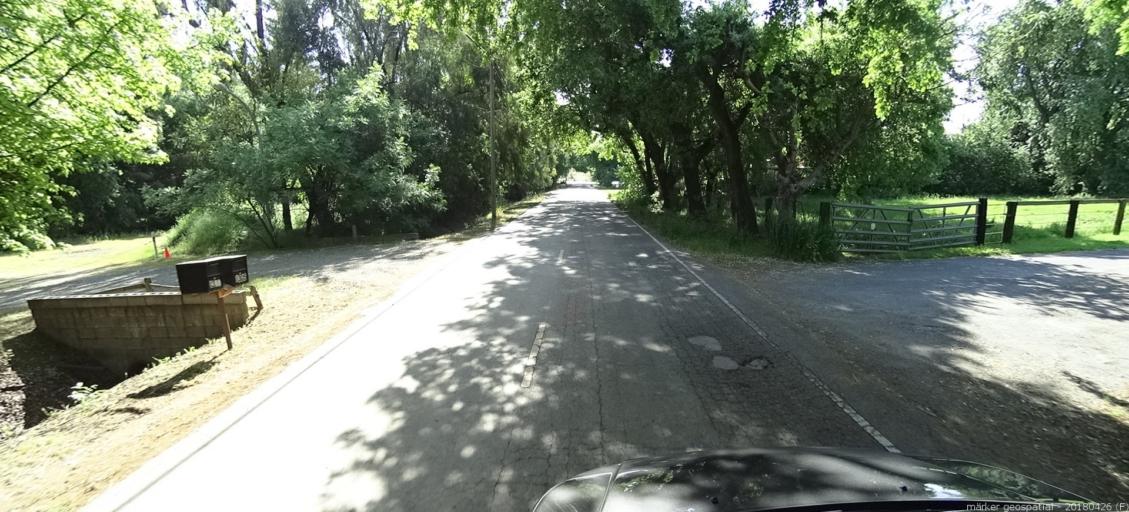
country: US
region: California
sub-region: Yolo County
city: West Sacramento
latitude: 38.5422
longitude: -121.5186
